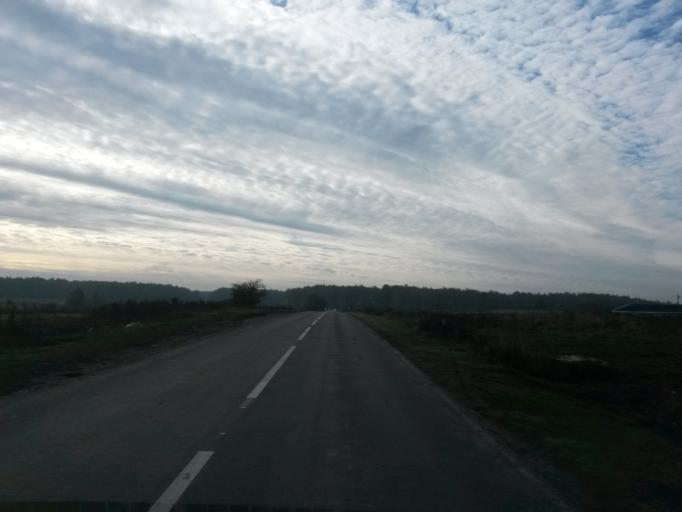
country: RU
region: Moskovskaya
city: Lyubuchany
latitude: 55.2383
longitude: 37.6428
